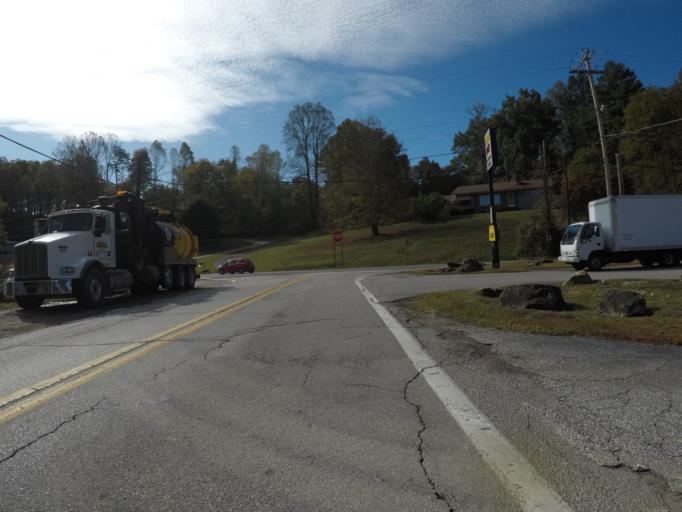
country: US
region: Ohio
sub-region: Lawrence County
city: Burlington
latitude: 38.3570
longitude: -82.5243
